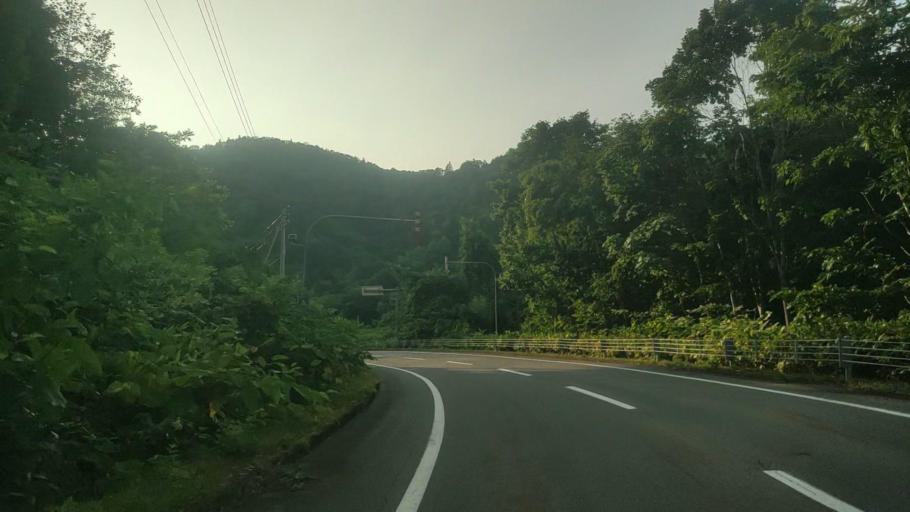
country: JP
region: Hokkaido
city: Bibai
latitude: 43.1803
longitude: 142.0661
